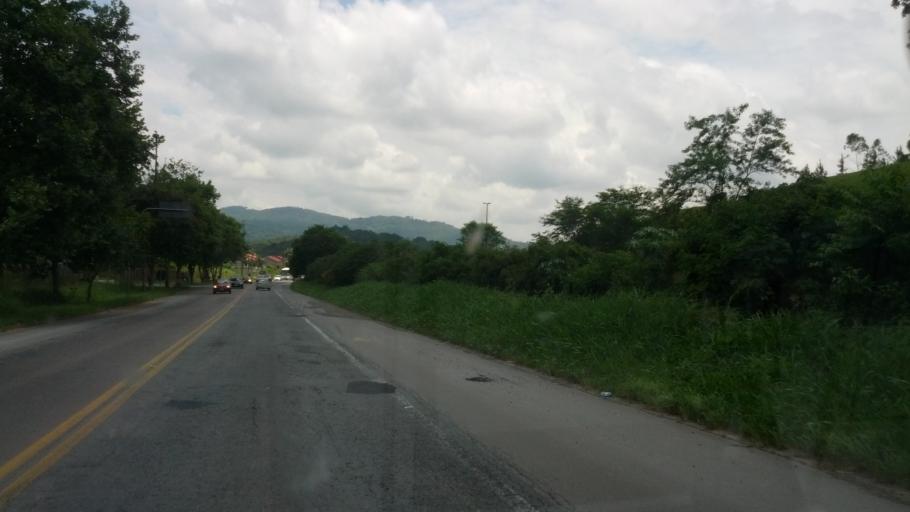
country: BR
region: Santa Catarina
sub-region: Blumenau
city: Blumenau
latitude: -26.8796
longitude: -49.1357
